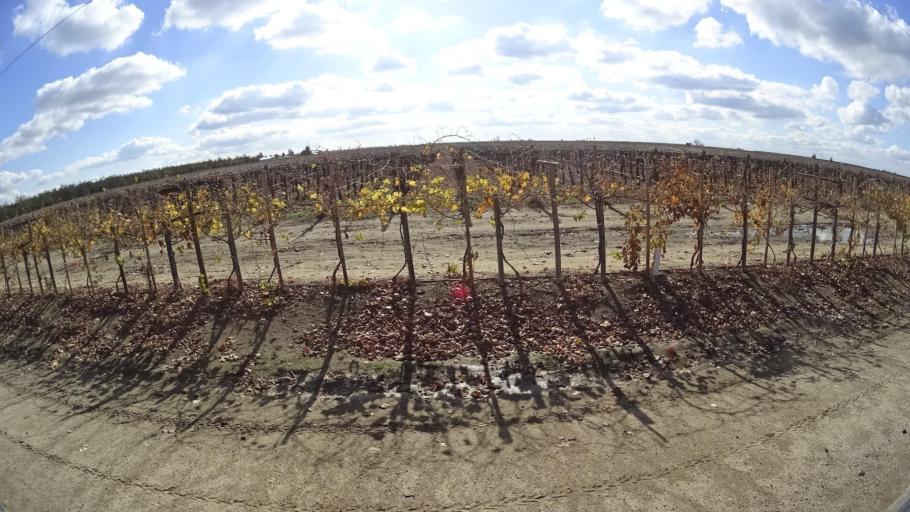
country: US
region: California
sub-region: Kern County
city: McFarland
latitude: 35.6888
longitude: -119.2446
